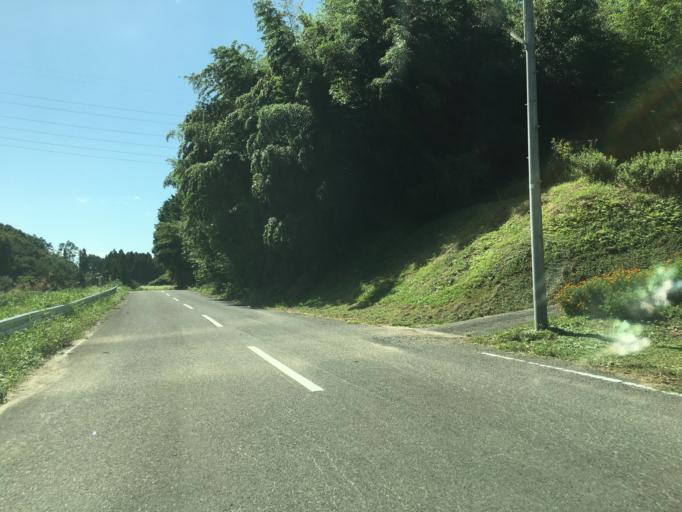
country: JP
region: Fukushima
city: Sukagawa
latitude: 37.2791
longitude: 140.4677
